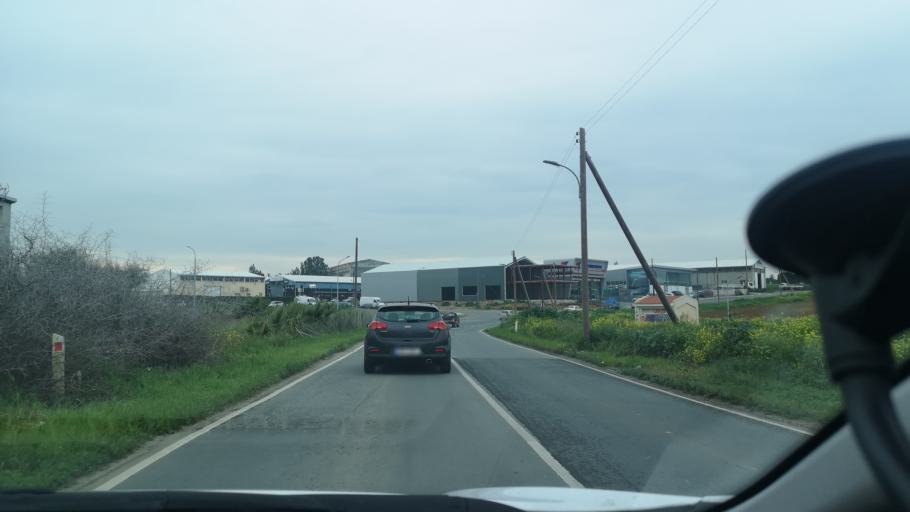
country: CY
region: Lefkosia
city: Tseri
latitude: 35.1039
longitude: 33.3329
